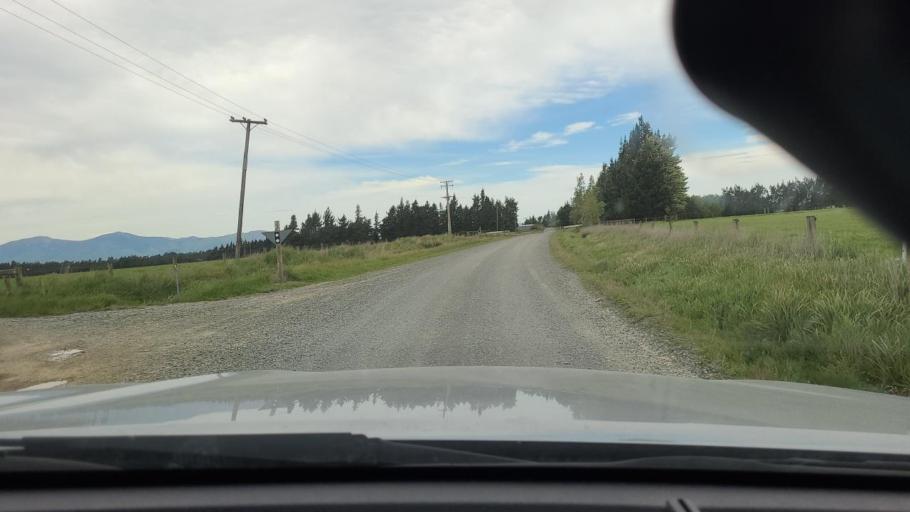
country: NZ
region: Southland
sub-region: Southland District
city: Te Anau
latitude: -45.6608
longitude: 168.1520
